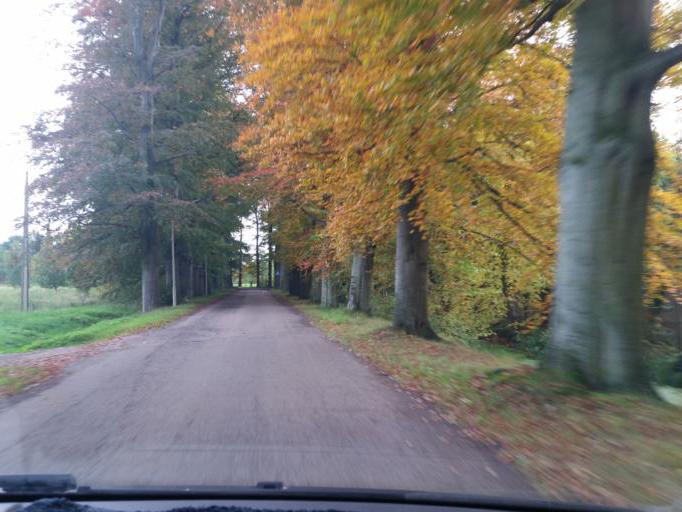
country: BE
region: Flanders
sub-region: Provincie Antwerpen
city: Lier
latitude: 51.1413
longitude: 4.5836
